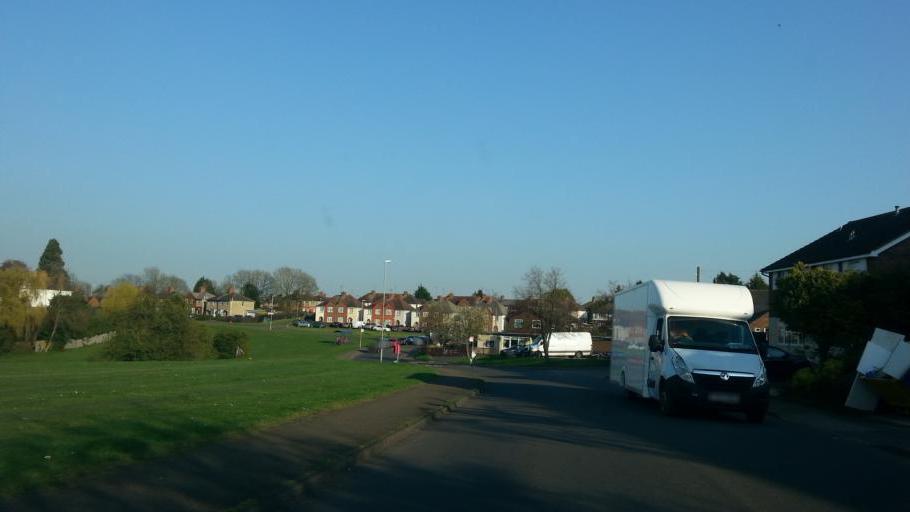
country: GB
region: England
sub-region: Northamptonshire
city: Rushden
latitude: 52.2912
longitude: -0.6189
